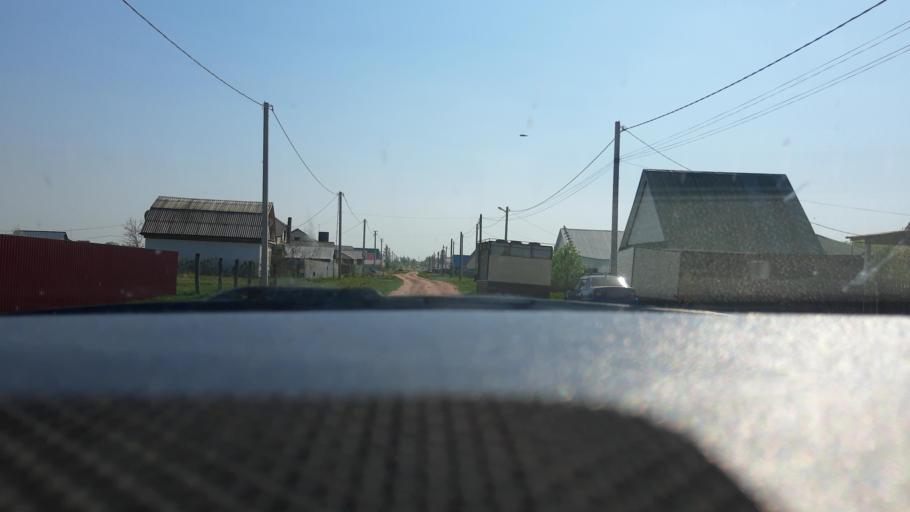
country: RU
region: Bashkortostan
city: Chishmy
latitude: 54.3961
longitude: 55.2103
